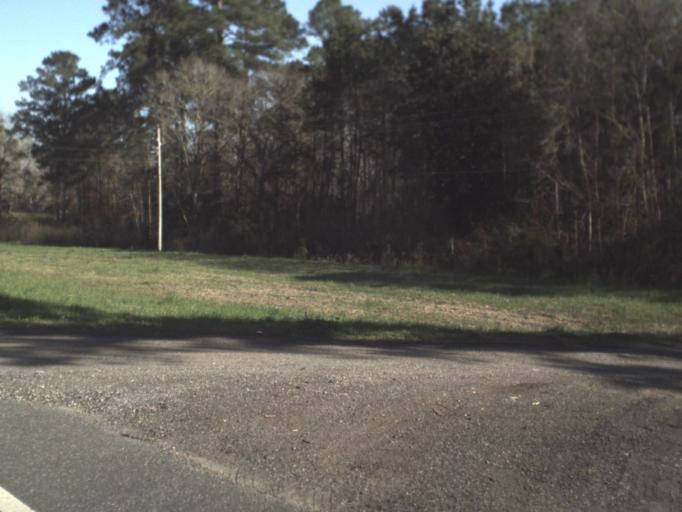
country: US
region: Florida
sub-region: Jackson County
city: Marianna
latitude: 30.7845
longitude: -85.2989
